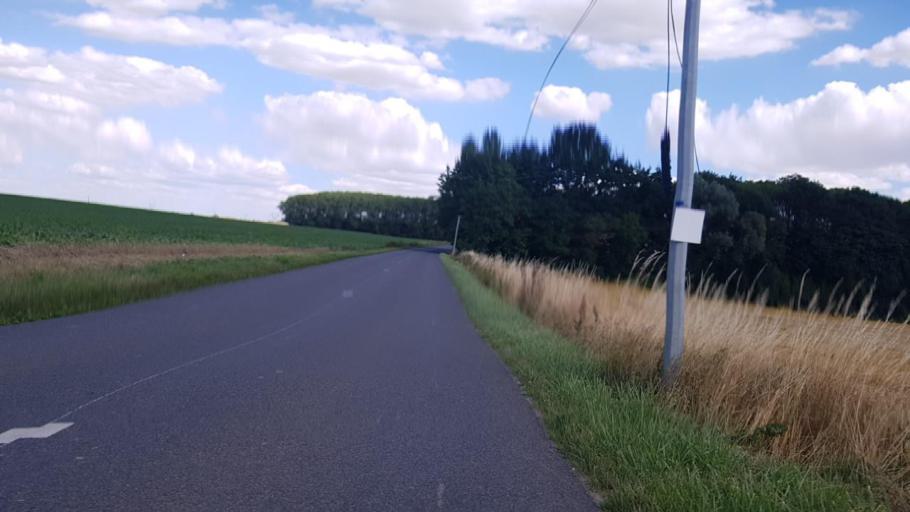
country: FR
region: Ile-de-France
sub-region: Departement de Seine-et-Marne
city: Moussy-le-Neuf
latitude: 49.0707
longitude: 2.6226
